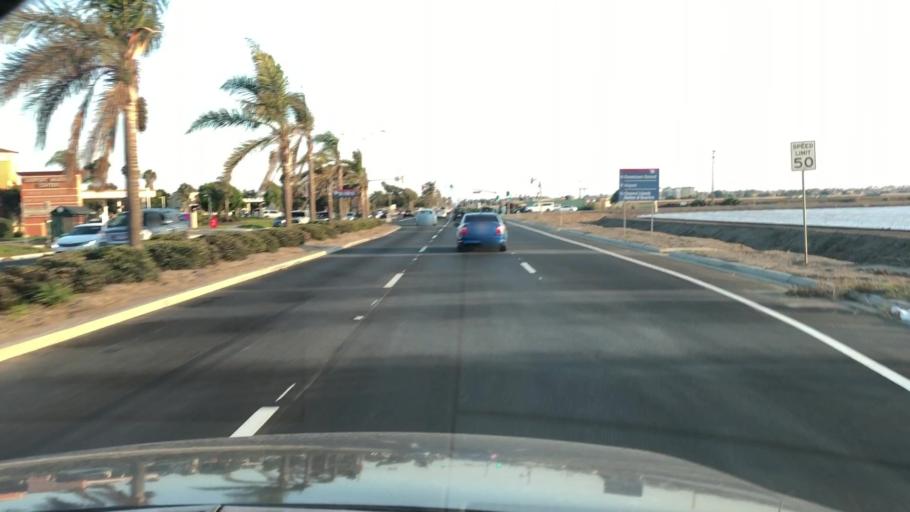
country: US
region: California
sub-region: Ventura County
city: Oxnard Shores
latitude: 34.1991
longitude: -119.2212
